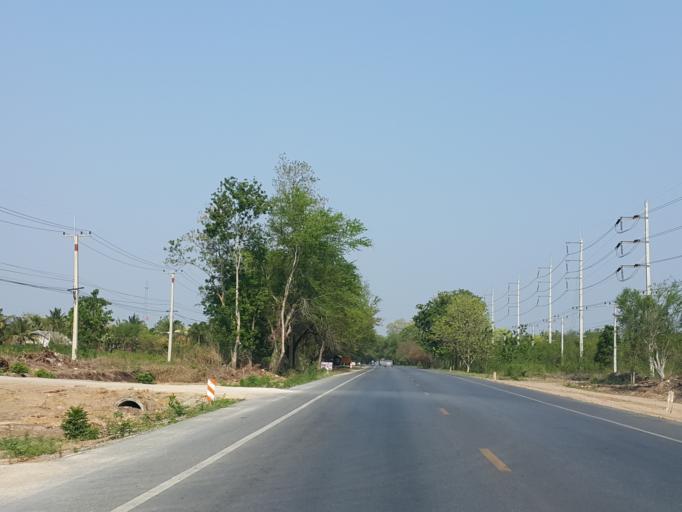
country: TH
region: Kanchanaburi
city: Sai Yok
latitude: 14.0897
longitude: 99.3160
